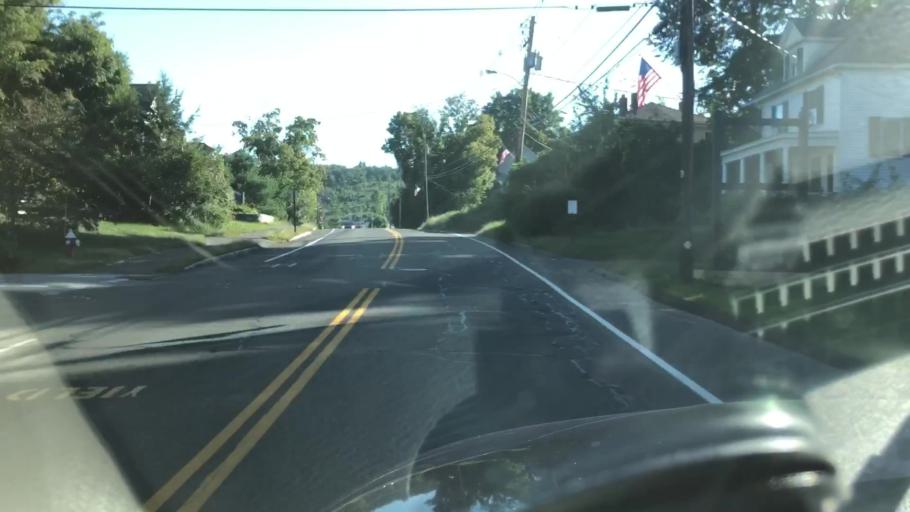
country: US
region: Massachusetts
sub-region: Hampden County
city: Monson
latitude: 42.1075
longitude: -72.3172
